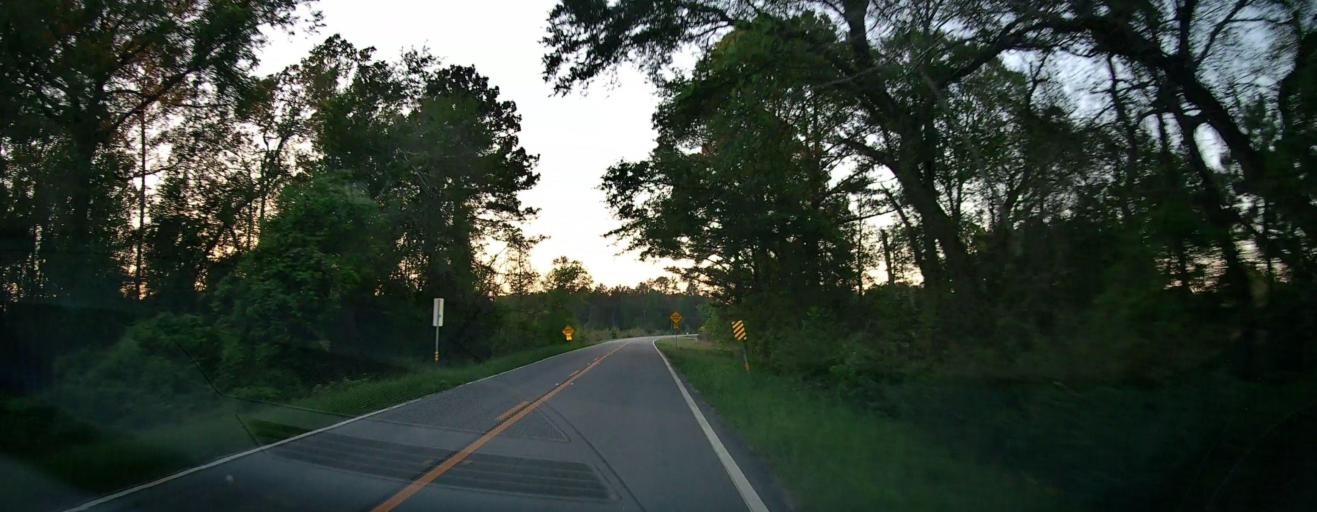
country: US
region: Georgia
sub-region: Wilcox County
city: Rochelle
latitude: 31.7990
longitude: -83.4500
